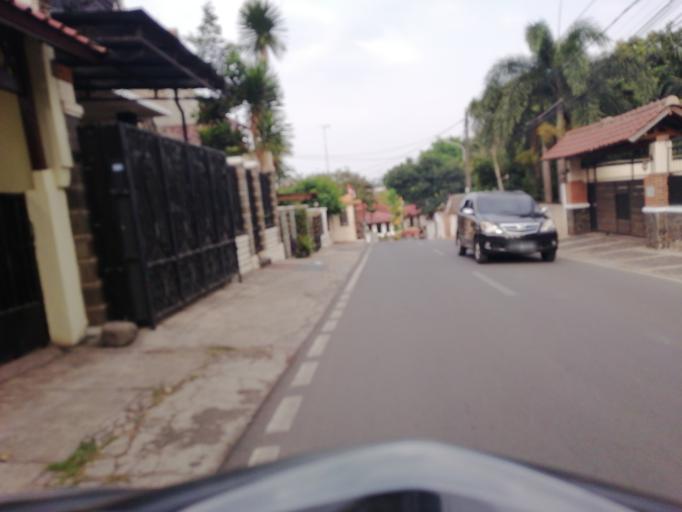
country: ID
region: West Java
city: Pamulang
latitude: -6.3042
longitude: 106.8009
